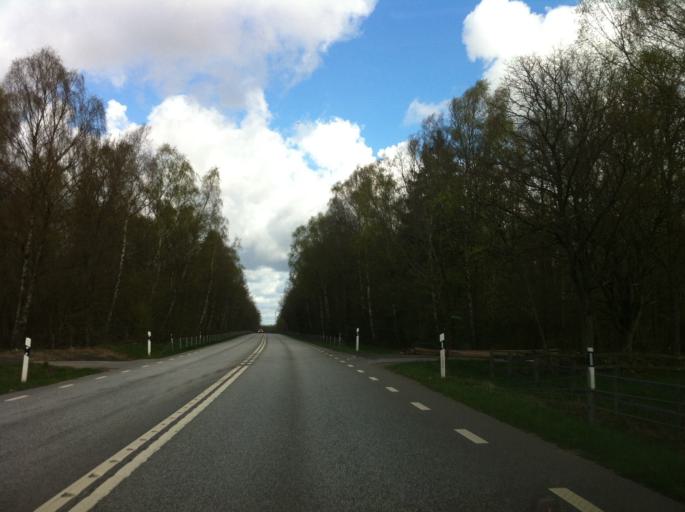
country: SE
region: Skane
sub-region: Horby Kommun
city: Hoerby
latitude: 55.8870
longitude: 13.6291
